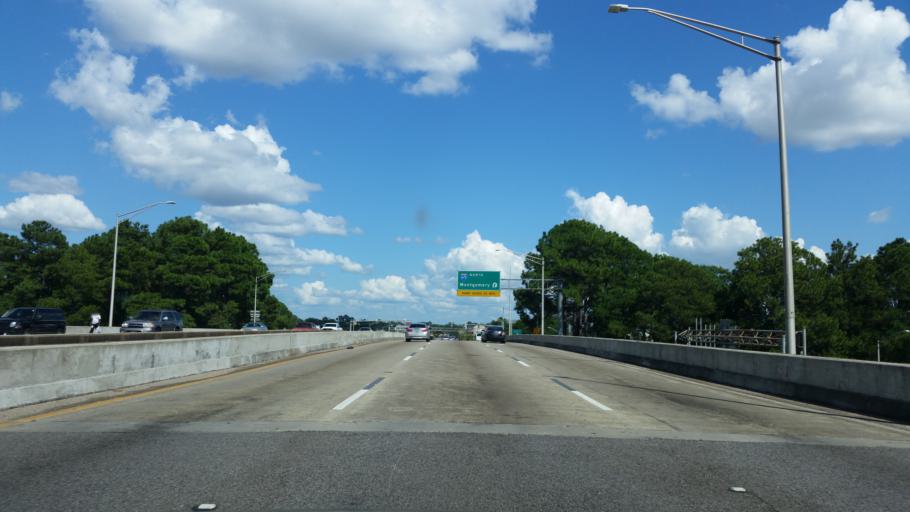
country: US
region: Alabama
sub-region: Mobile County
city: Prichard
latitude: 30.6761
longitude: -88.1279
